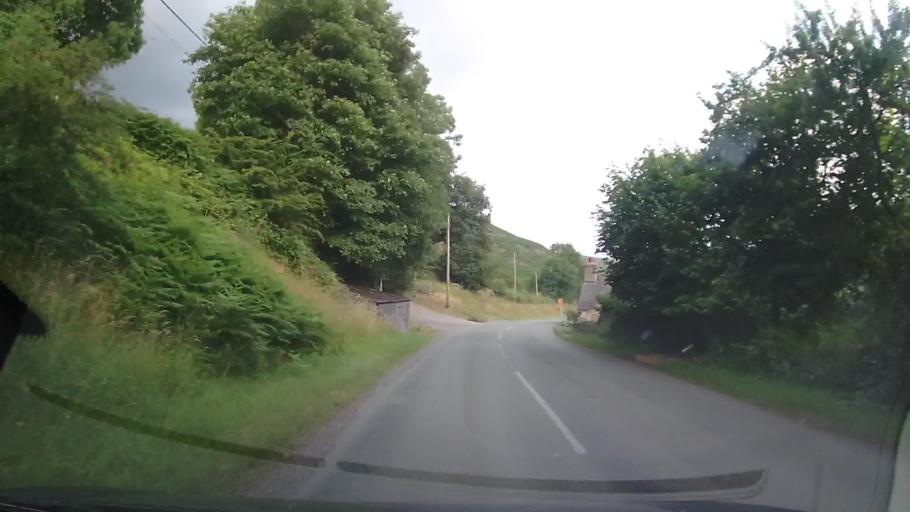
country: GB
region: Wales
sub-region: Sir Powys
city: Llangynog
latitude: 52.8382
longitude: -3.4205
